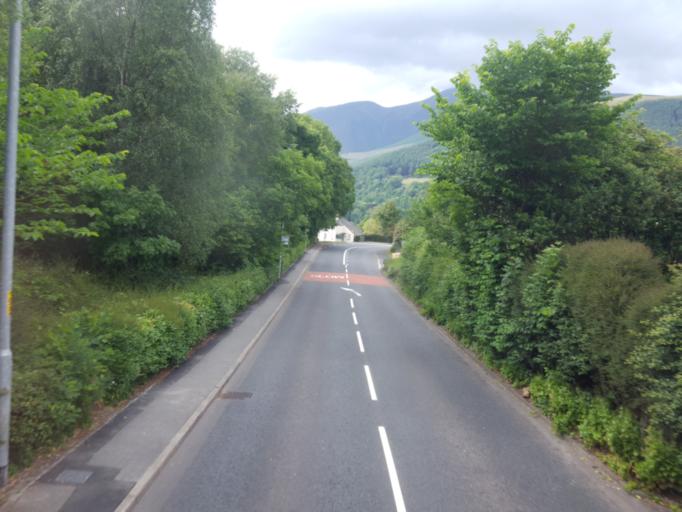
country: GB
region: England
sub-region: Cumbria
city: Keswick
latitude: 54.5977
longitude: -3.1174
